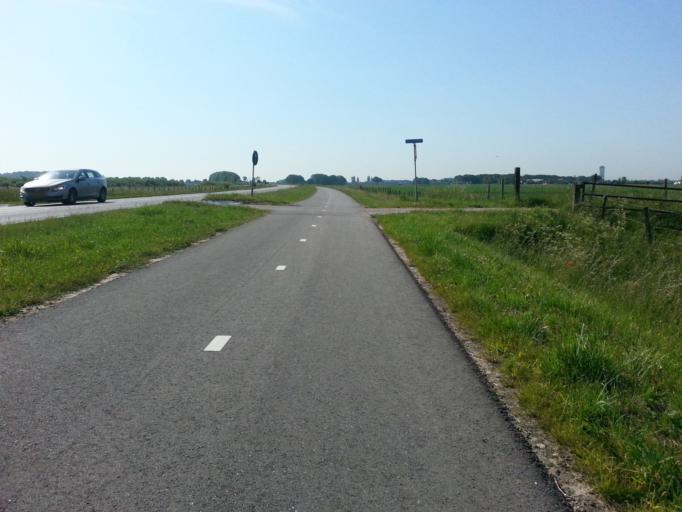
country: NL
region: Utrecht
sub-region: Gemeente Utrechtse Heuvelrug
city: Driebergen-Rijsenburg
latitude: 52.0175
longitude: 5.2620
